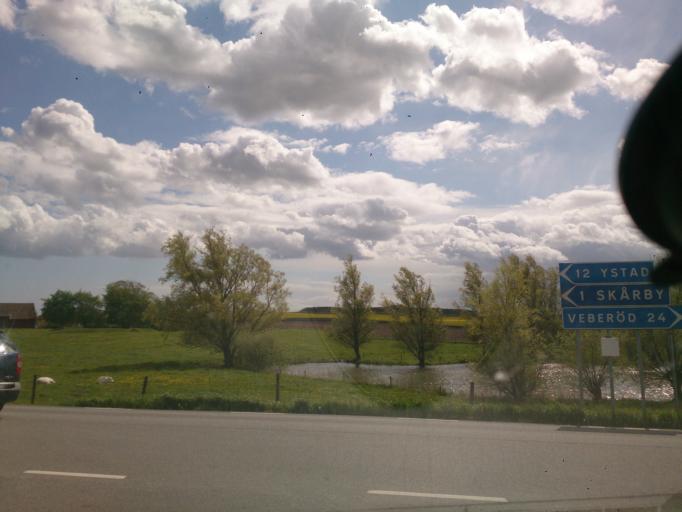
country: SE
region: Skane
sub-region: Ystads Kommun
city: Ystad
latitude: 55.4904
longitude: 13.7103
